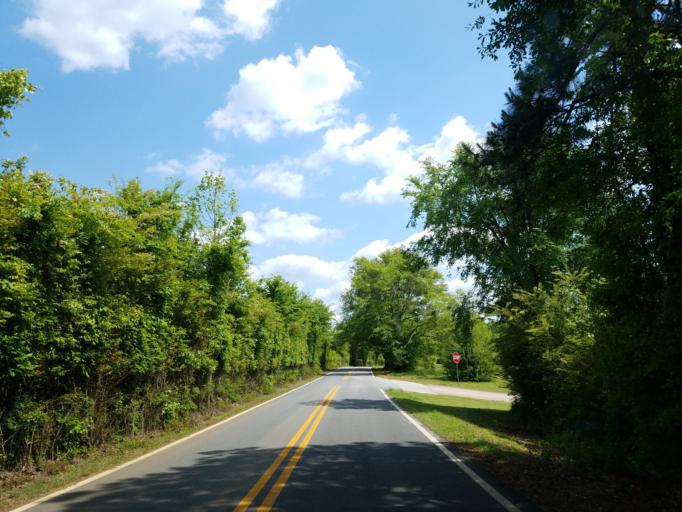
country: US
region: Georgia
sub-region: Monroe County
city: Forsyth
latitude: 33.0863
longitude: -83.9585
